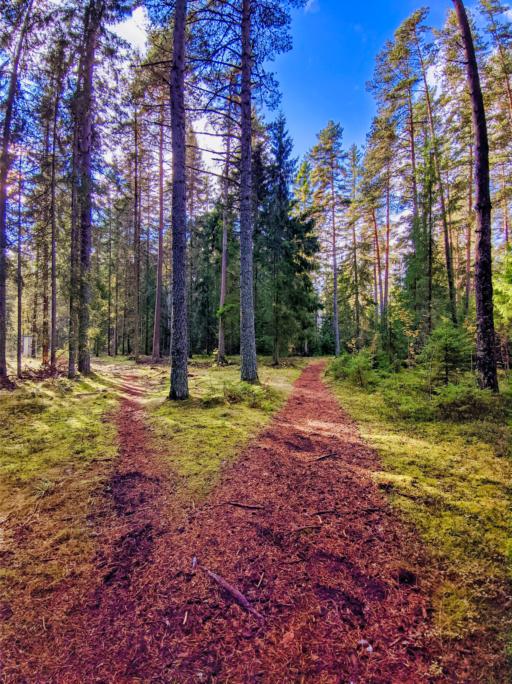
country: NO
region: Akershus
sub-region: Nannestad
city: Teigebyen
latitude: 60.2121
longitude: 11.0795
